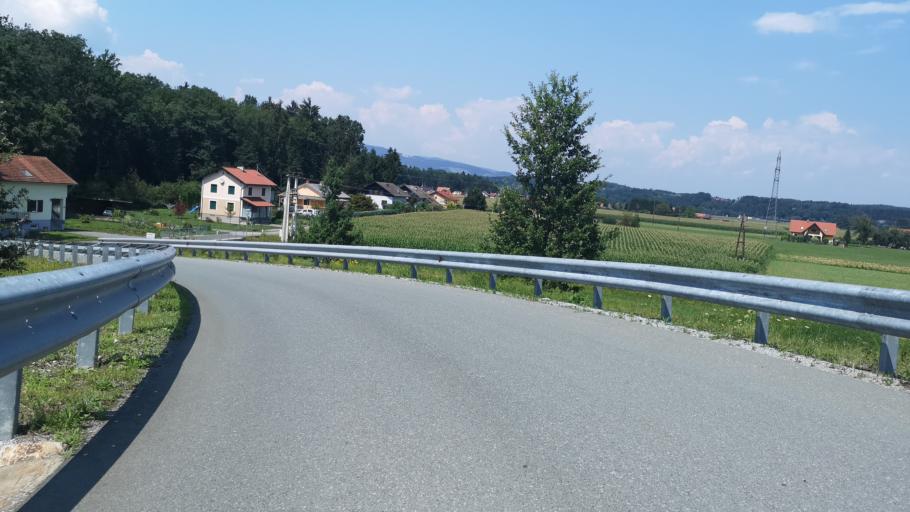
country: AT
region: Styria
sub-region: Politischer Bezirk Deutschlandsberg
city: Unterbergla
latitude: 46.8128
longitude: 15.2719
